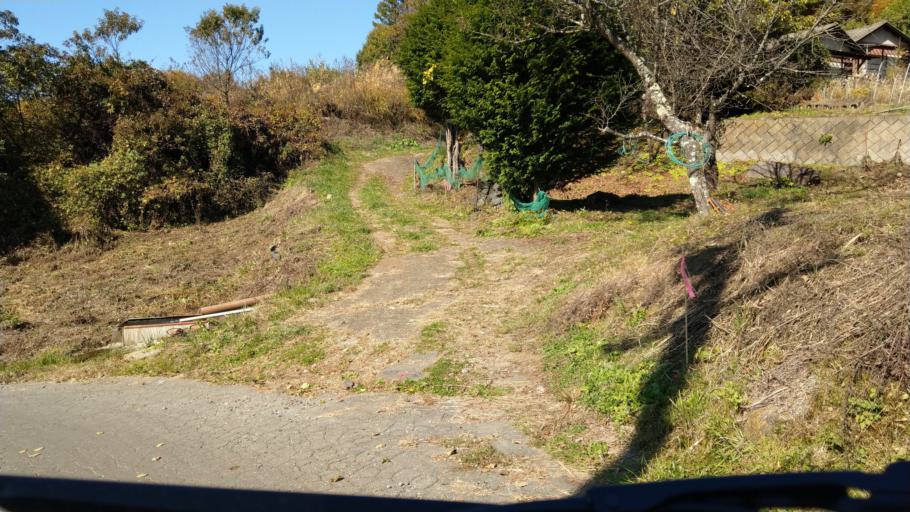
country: JP
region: Nagano
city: Komoro
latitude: 36.3587
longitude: 138.4489
